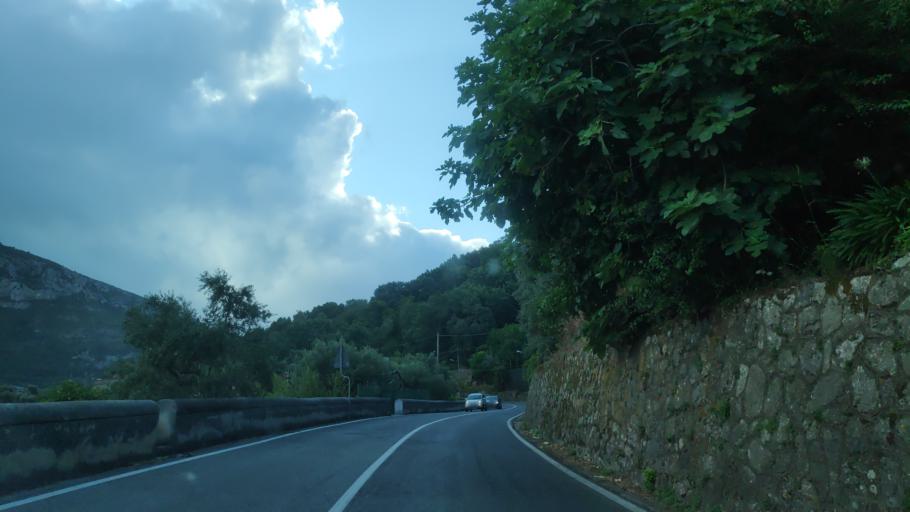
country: IT
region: Campania
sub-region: Provincia di Napoli
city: Piano di Sorrento
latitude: 40.6209
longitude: 14.4163
